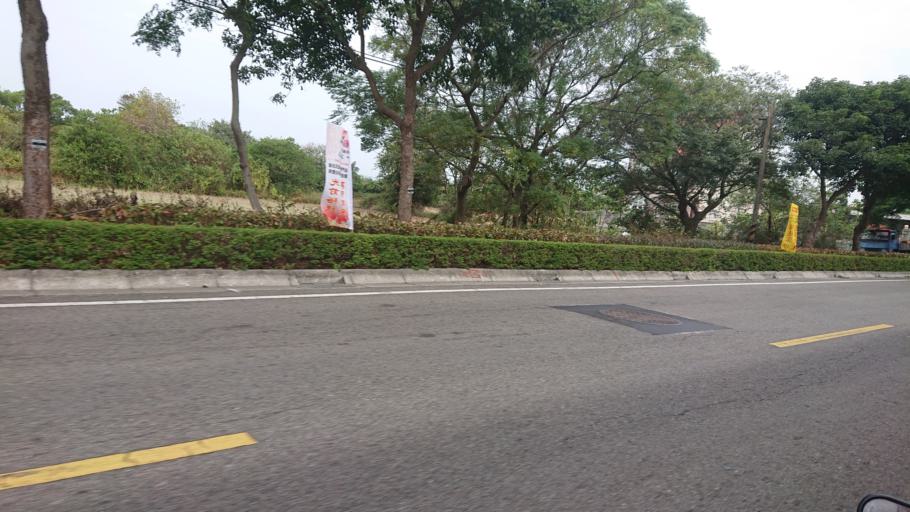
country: TW
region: Fukien
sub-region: Kinmen
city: Jincheng
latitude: 24.4129
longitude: 118.3021
